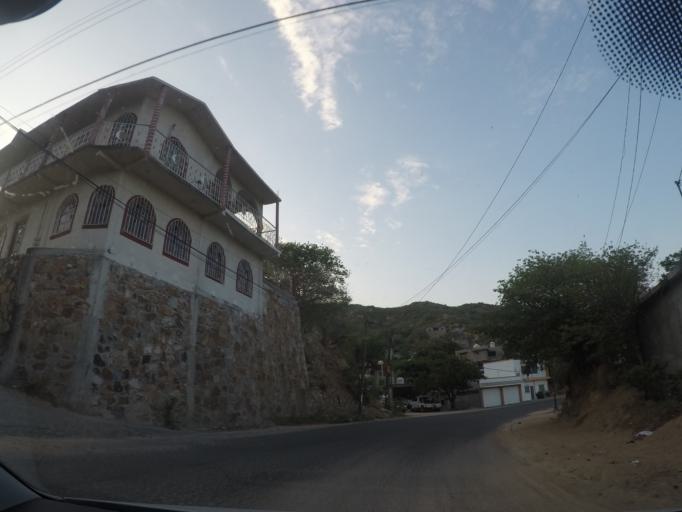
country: MX
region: Oaxaca
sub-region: Salina Cruz
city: Salina Cruz
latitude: 16.1924
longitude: -95.2099
